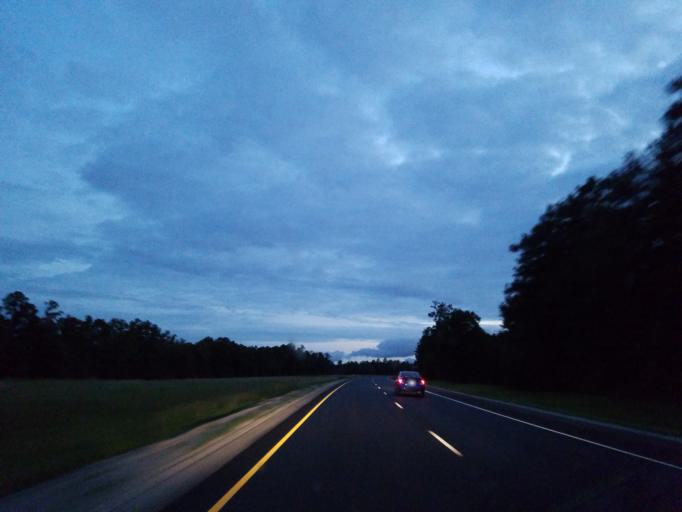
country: US
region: Mississippi
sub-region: Clarke County
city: Stonewall
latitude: 32.0207
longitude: -88.9237
